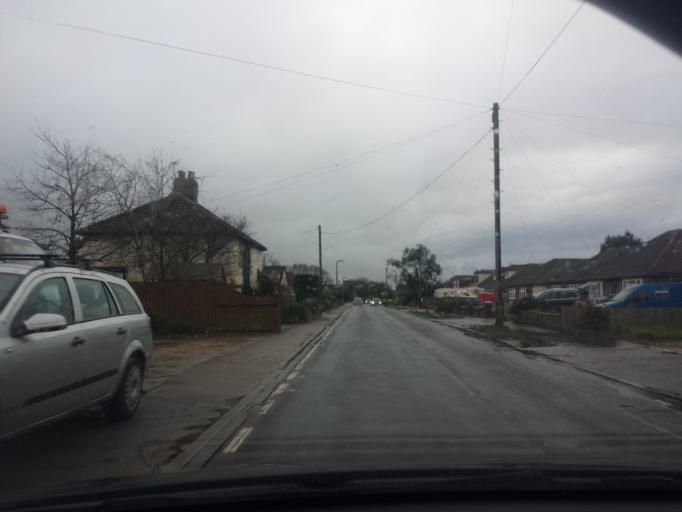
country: GB
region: England
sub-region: Essex
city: Little Clacton
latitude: 51.8057
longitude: 1.1273
